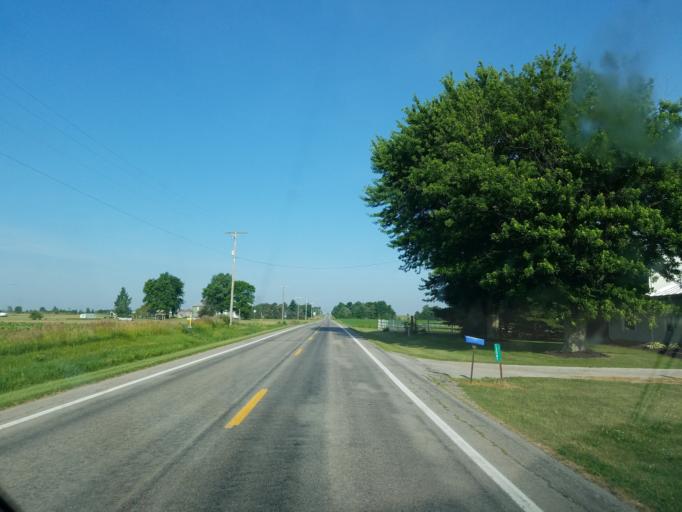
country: US
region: Ohio
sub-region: Hardin County
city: Kenton
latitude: 40.7317
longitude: -83.6327
